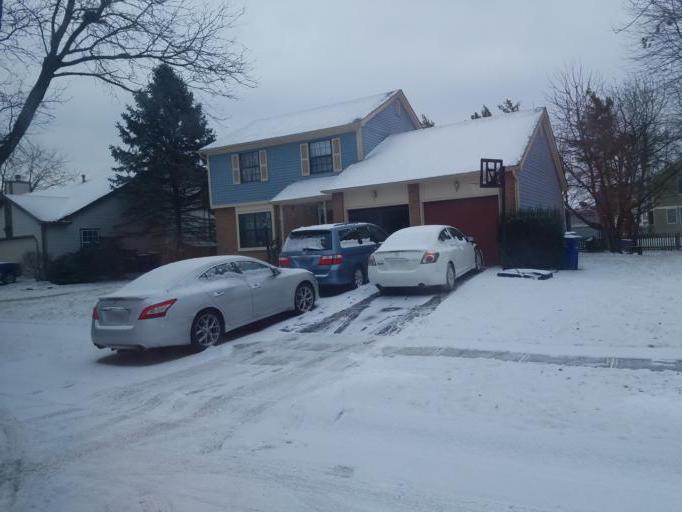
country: US
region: Ohio
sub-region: Franklin County
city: Dublin
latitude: 40.1156
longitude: -83.0802
